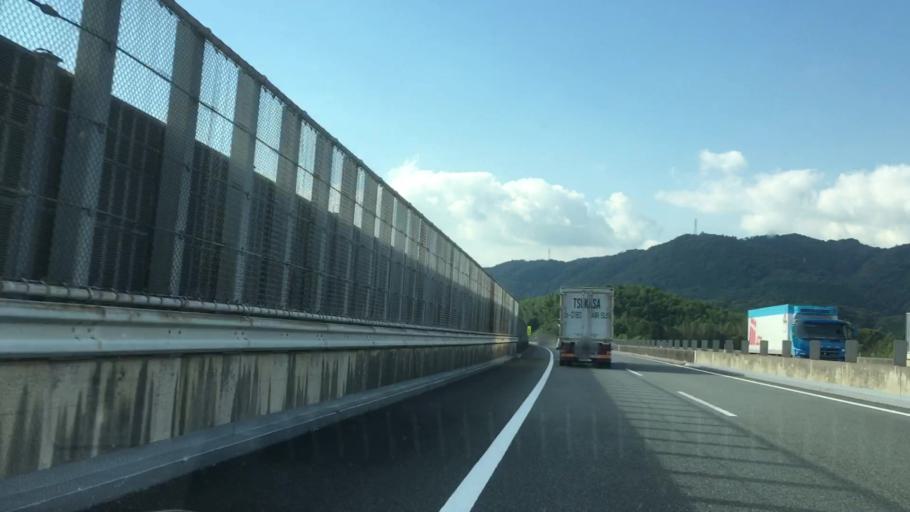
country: JP
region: Yamaguchi
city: Kudamatsu
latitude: 34.0381
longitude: 131.9243
